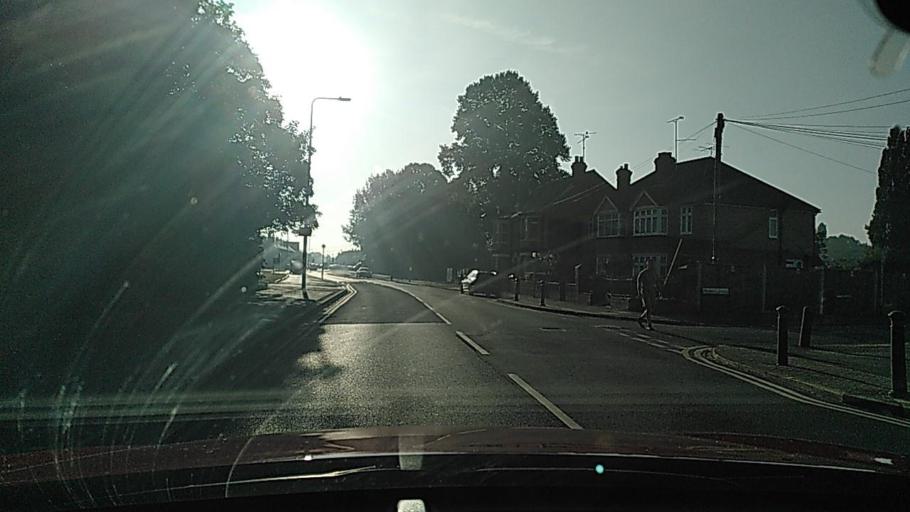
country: GB
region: England
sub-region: Reading
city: Reading
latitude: 51.4664
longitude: -0.9690
